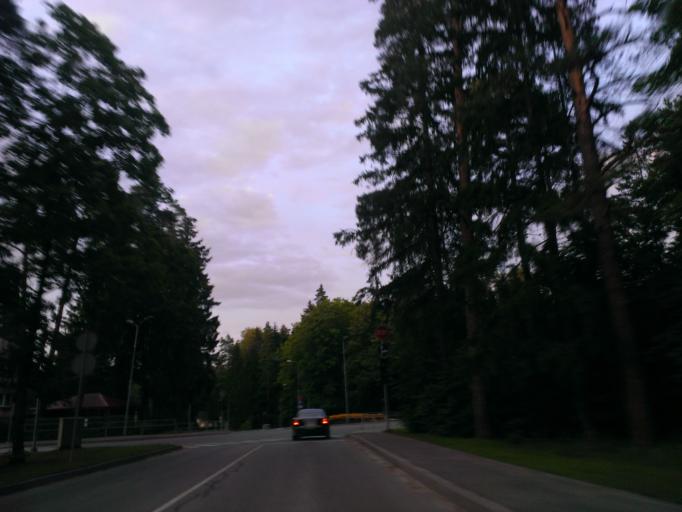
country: LV
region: Ogre
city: Ogre
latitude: 56.8197
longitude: 24.6107
